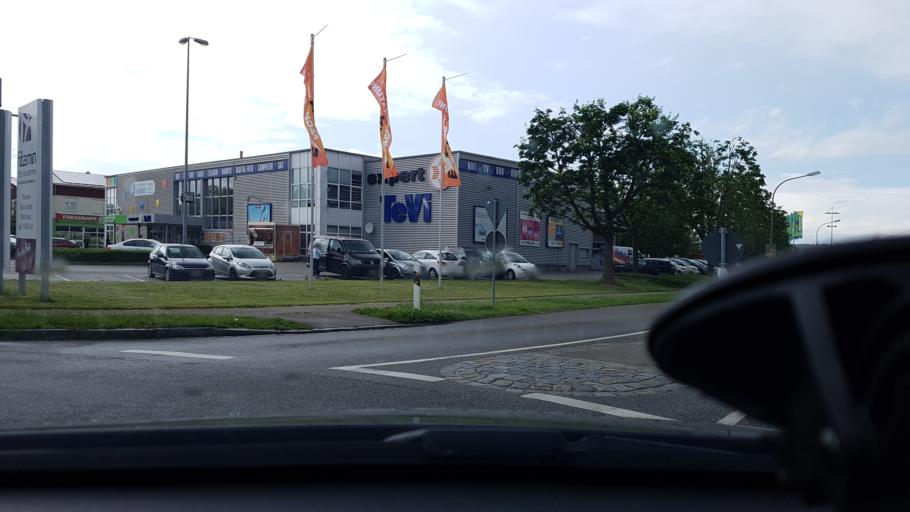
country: DE
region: Bavaria
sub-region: Upper Bavaria
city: Neuotting
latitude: 48.2426
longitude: 12.7086
